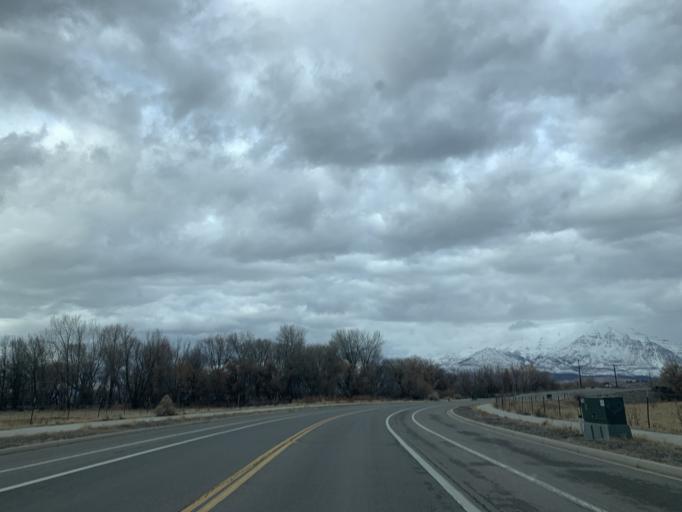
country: US
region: Utah
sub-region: Utah County
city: Provo
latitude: 40.2376
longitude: -111.7133
